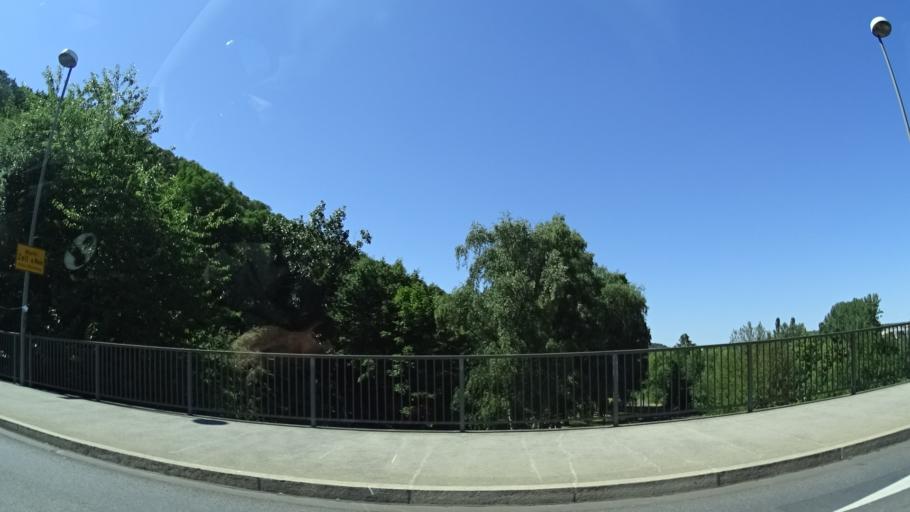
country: DE
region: Bavaria
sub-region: Regierungsbezirk Unterfranken
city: Zell am Main
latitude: 49.8041
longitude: 9.8775
